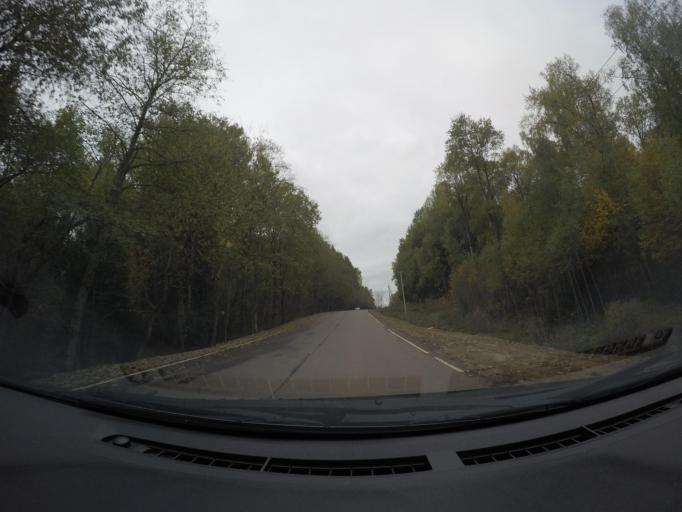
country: RU
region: Moskovskaya
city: Ruza
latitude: 55.7894
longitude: 36.2494
